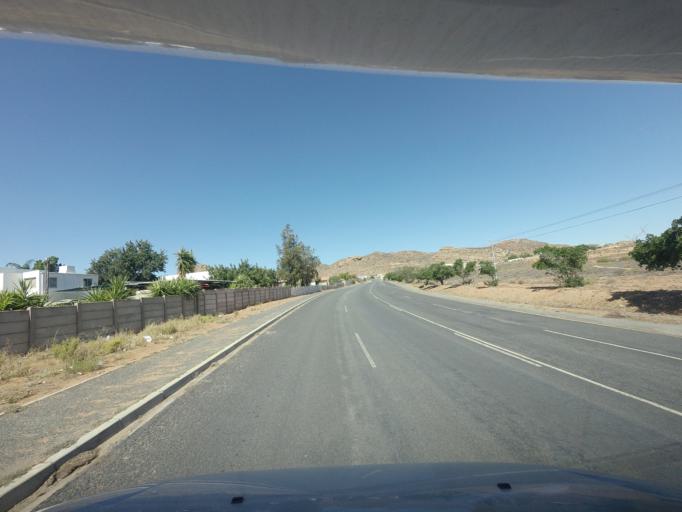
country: ZA
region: Northern Cape
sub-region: Namakwa District Municipality
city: Springbok
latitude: -29.6614
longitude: 17.8936
